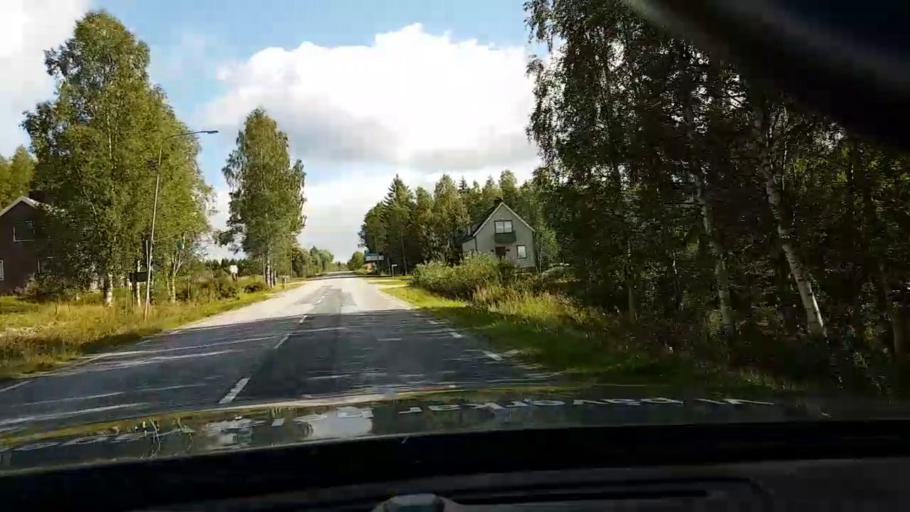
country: SE
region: Vaesterbotten
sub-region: Asele Kommun
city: Asele
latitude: 63.7865
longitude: 17.6483
